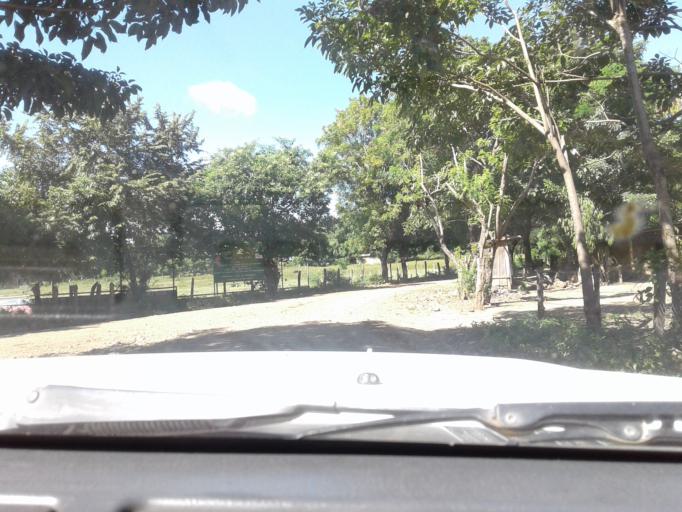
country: NI
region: Rivas
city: Tola
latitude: 11.5235
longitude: -86.0729
